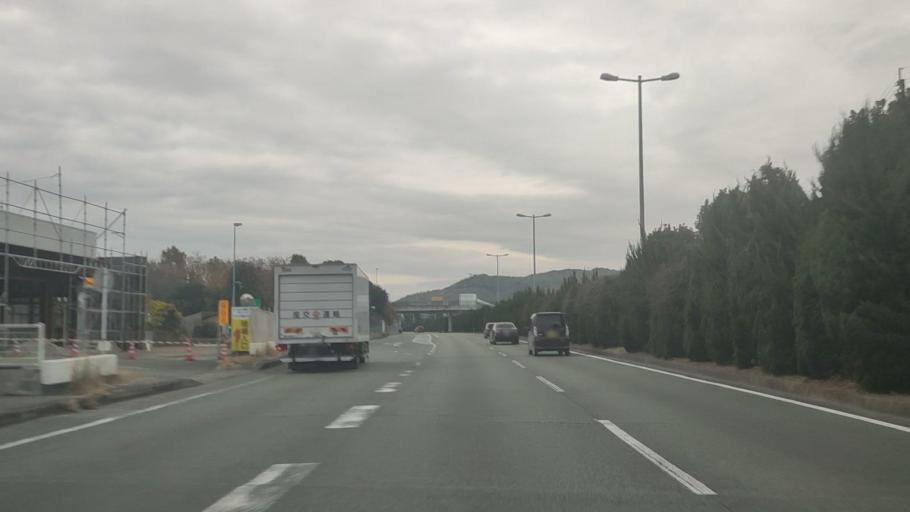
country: JP
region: Kumamoto
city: Kumamoto
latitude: 32.8321
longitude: 130.7737
